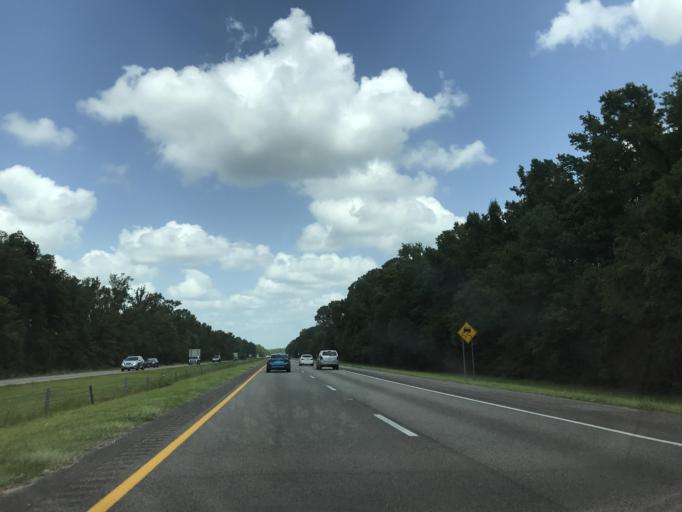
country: US
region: North Carolina
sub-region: Pender County
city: Rocky Point
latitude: 34.4482
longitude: -77.8763
